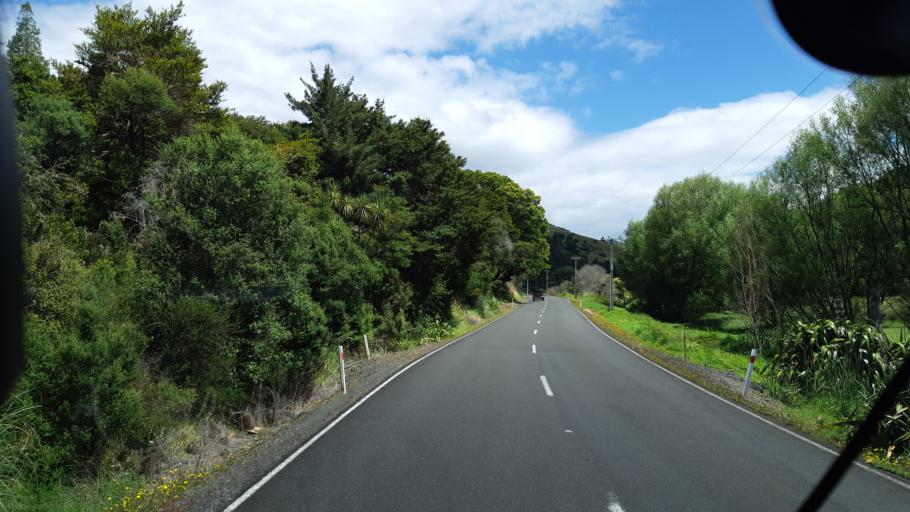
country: NZ
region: Northland
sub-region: Far North District
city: Taipa
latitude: -35.2715
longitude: 173.5069
